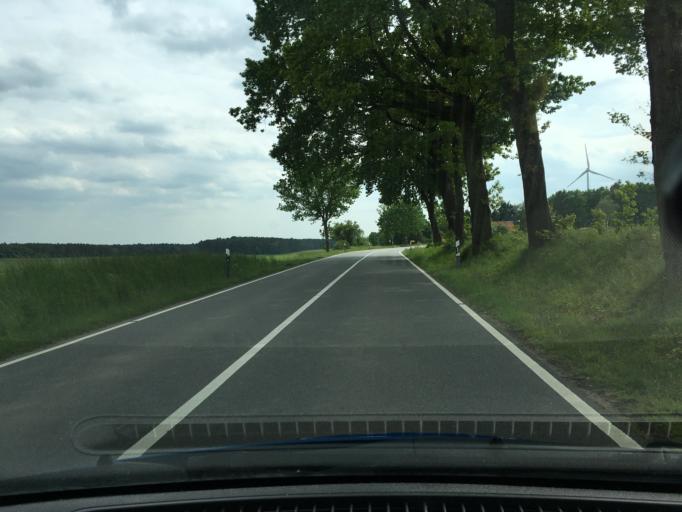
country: DE
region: Lower Saxony
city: Betzendorf
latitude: 53.1073
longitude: 10.3003
